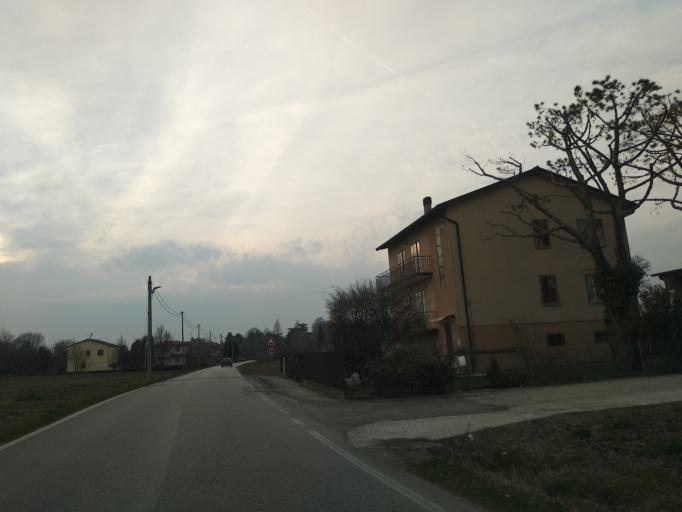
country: IT
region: Veneto
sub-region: Provincia di Vicenza
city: Villaggio Montegrappa
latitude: 45.5573
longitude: 11.6091
